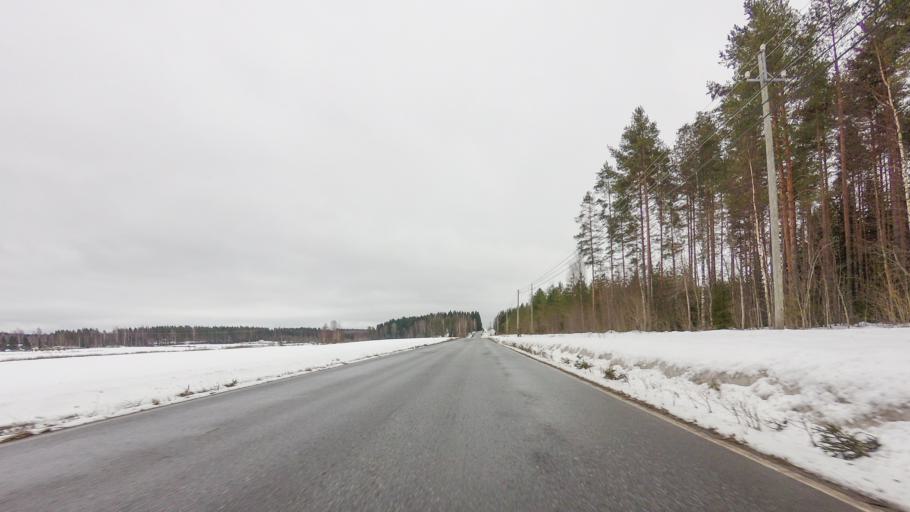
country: FI
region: Southern Savonia
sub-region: Savonlinna
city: Savonlinna
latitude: 61.9522
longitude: 28.8561
